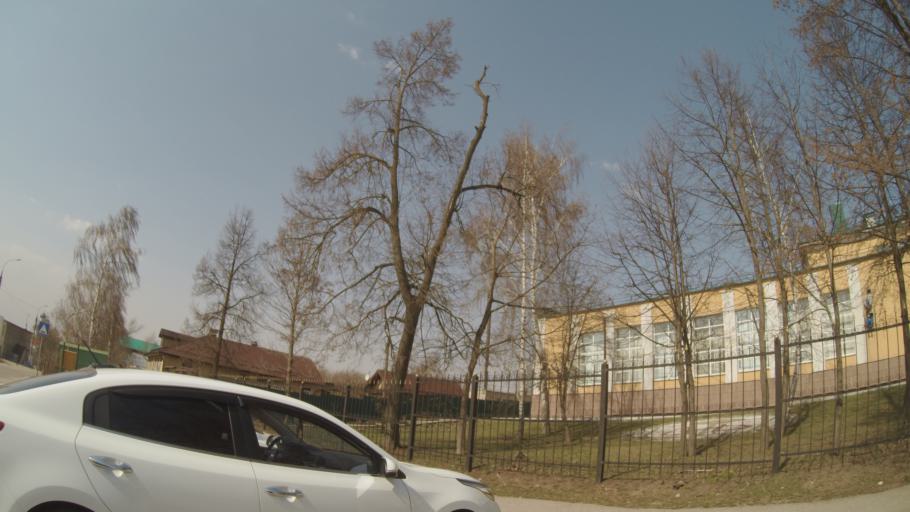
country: RU
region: Nizjnij Novgorod
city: Arzamas
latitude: 55.3853
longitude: 43.8206
